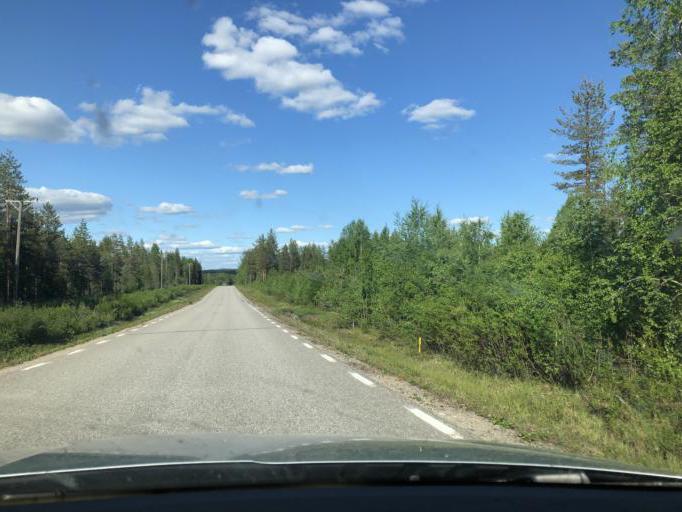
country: SE
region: Norrbotten
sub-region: Kalix Kommun
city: Kalix
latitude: 66.1020
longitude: 23.2776
